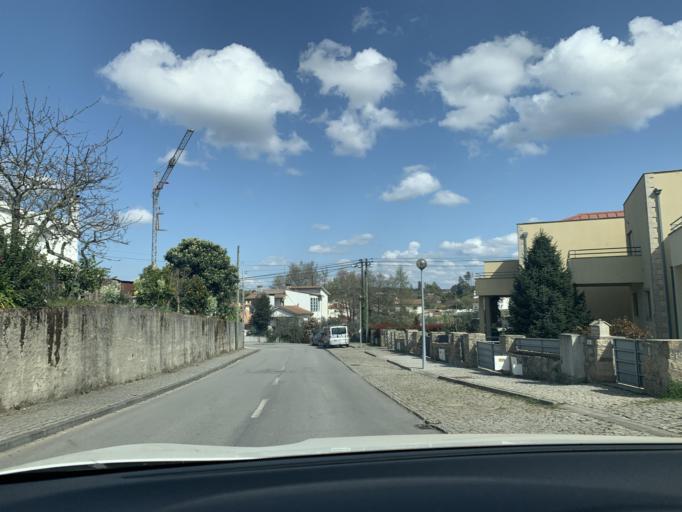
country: PT
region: Viseu
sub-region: Viseu
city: Rio de Loba
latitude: 40.6739
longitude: -7.8814
